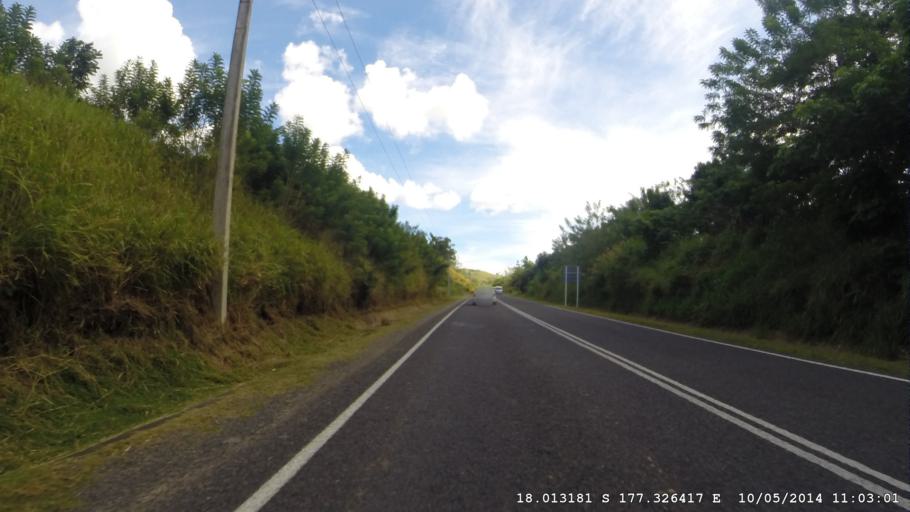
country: FJ
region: Western
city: Nadi
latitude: -18.0132
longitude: 177.3264
